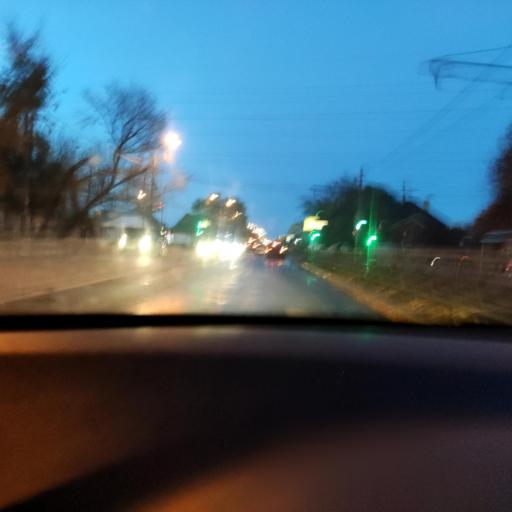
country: RU
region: Samara
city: Samara
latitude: 53.1952
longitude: 50.2181
